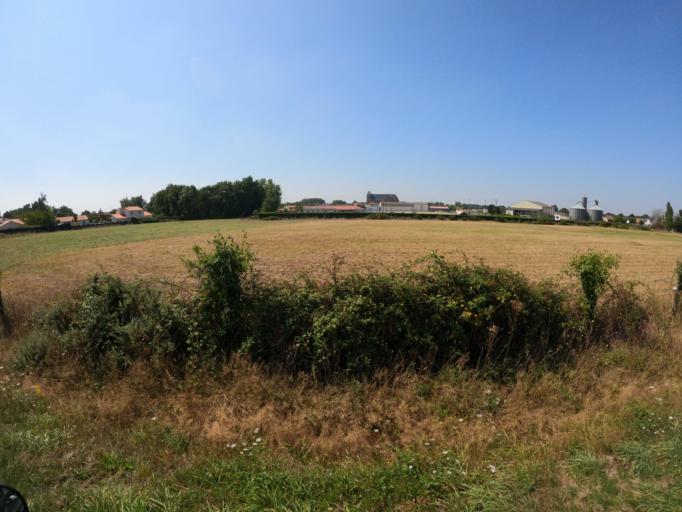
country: FR
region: Pays de la Loire
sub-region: Departement de la Loire-Atlantique
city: La Planche
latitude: 47.0197
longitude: -1.4320
